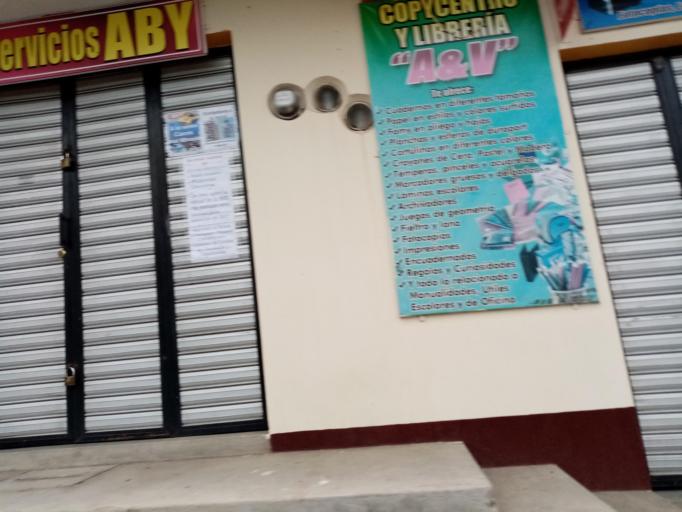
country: GT
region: Quetzaltenango
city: Quetzaltenango
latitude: 14.8530
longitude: -91.5151
